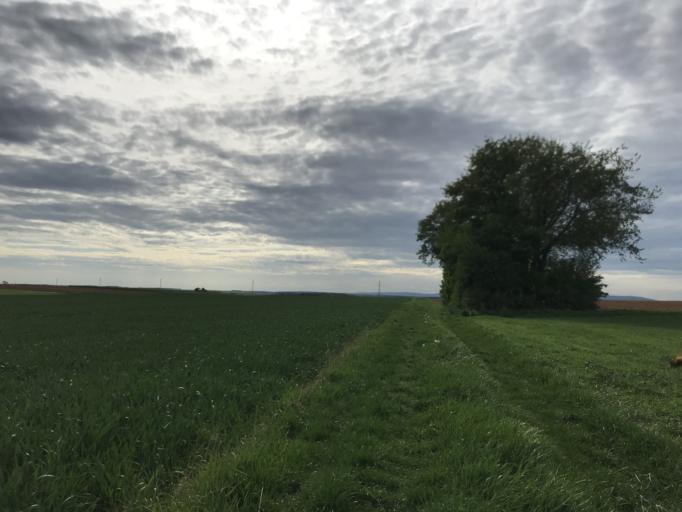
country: DE
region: Rheinland-Pfalz
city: Essenheim
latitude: 49.9471
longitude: 8.1482
